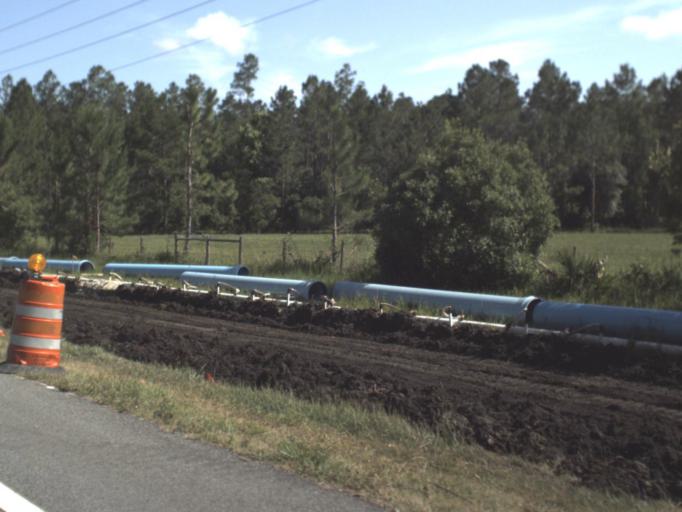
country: US
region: Florida
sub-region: Saint Johns County
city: Saint Augustine
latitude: 29.9384
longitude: -81.4371
